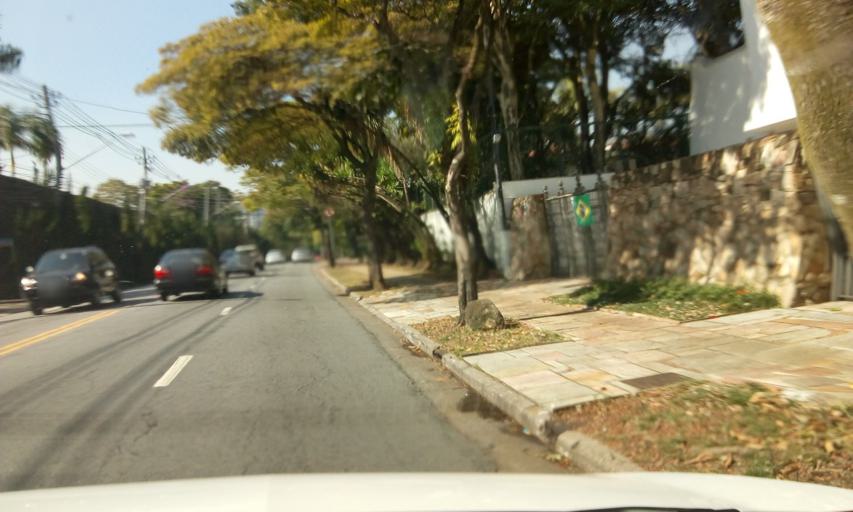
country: BR
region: Sao Paulo
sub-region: Sao Paulo
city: Sao Paulo
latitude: -23.5981
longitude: -46.7081
